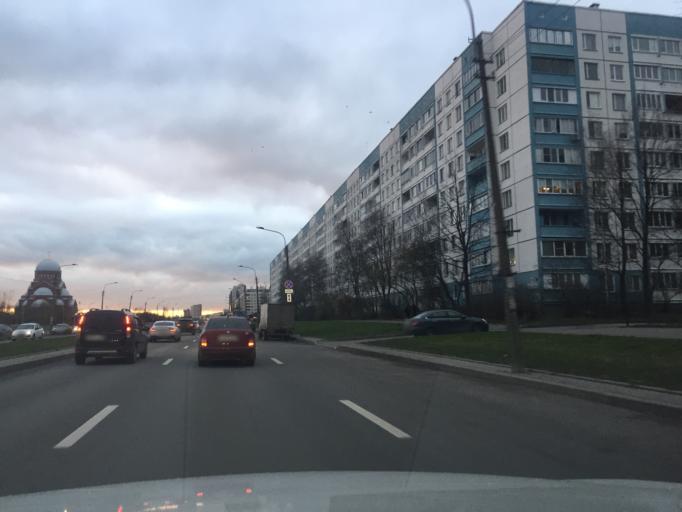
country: RU
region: St.-Petersburg
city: Grazhdanka
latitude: 60.0240
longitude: 30.4170
